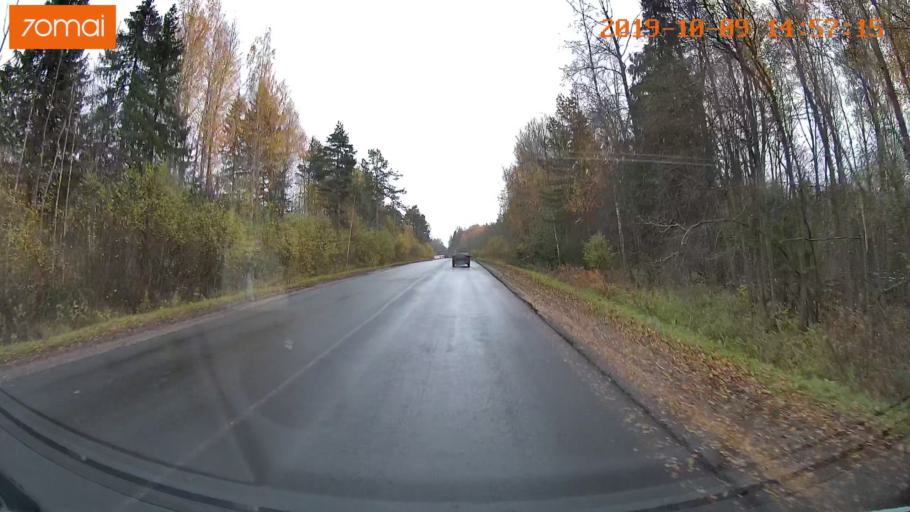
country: RU
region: Kostroma
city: Chistyye Bory
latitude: 58.3394
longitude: 41.6499
